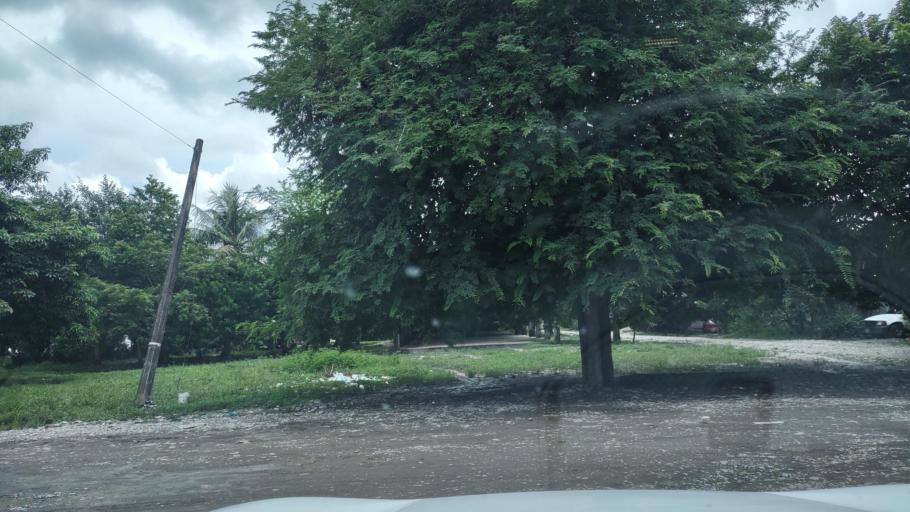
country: MX
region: Veracruz
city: Alamo
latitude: 20.9593
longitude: -97.7055
